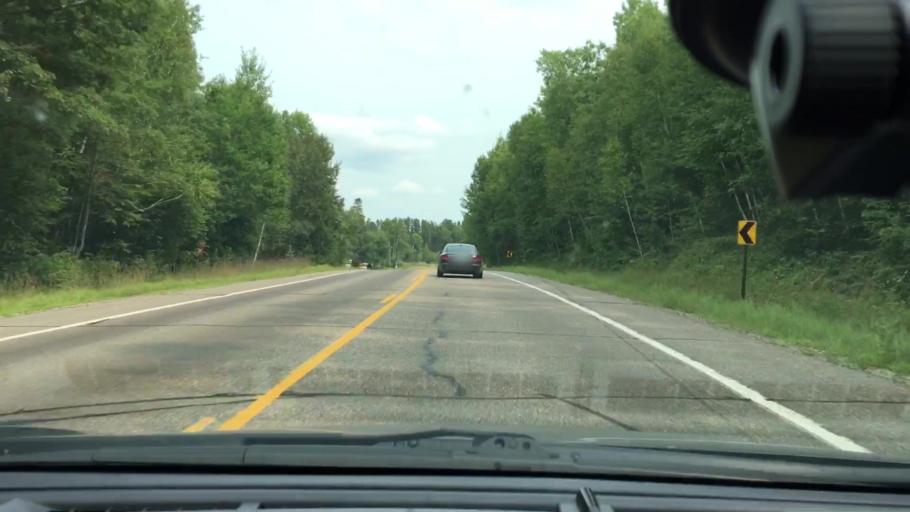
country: US
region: Minnesota
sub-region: Crow Wing County
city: Cross Lake
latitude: 46.7310
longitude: -94.0043
